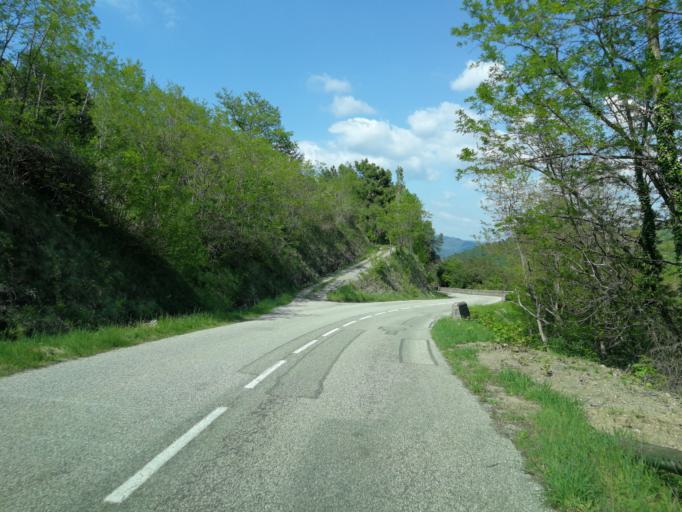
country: FR
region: Rhone-Alpes
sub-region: Departement de l'Ardeche
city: Saint-Sauveur-de-Montagut
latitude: 44.7908
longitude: 4.6109
